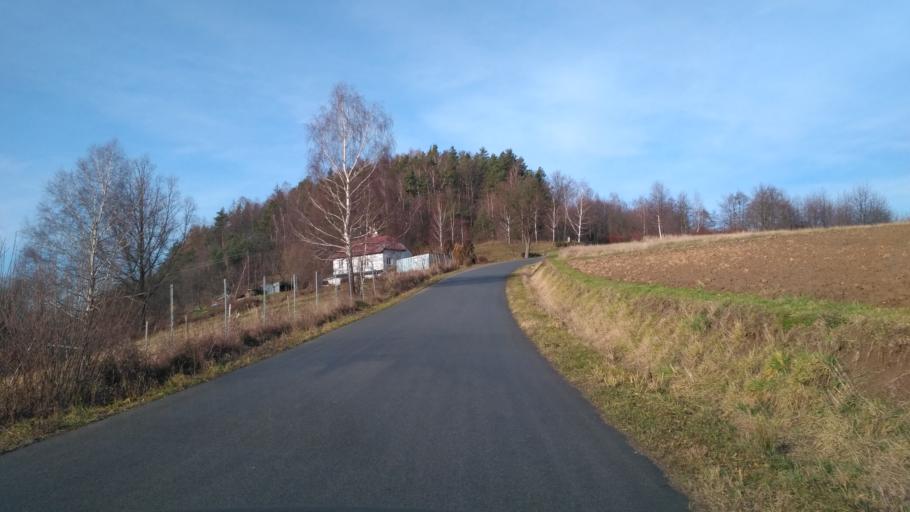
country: PL
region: Subcarpathian Voivodeship
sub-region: Powiat krosnienski
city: Korczyna
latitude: 49.7276
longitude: 21.7928
